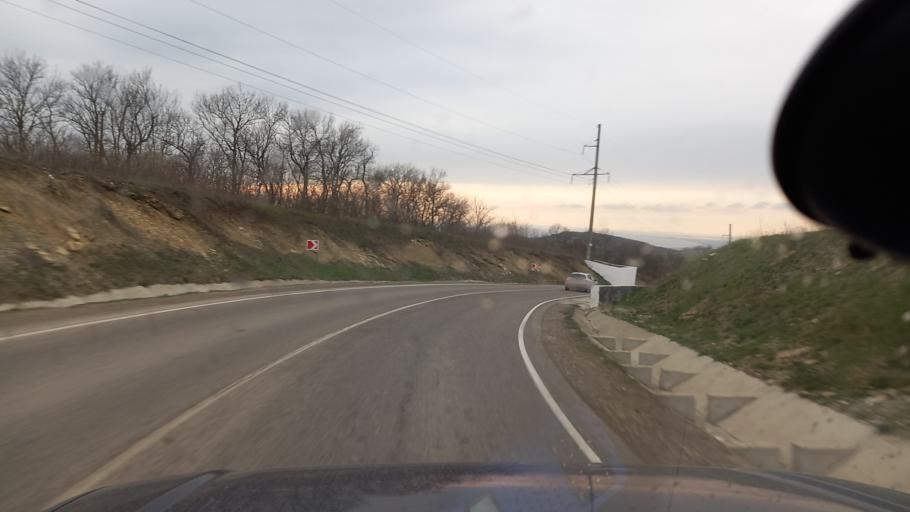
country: RU
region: Krasnodarskiy
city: Sukko
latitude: 44.8394
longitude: 37.4024
